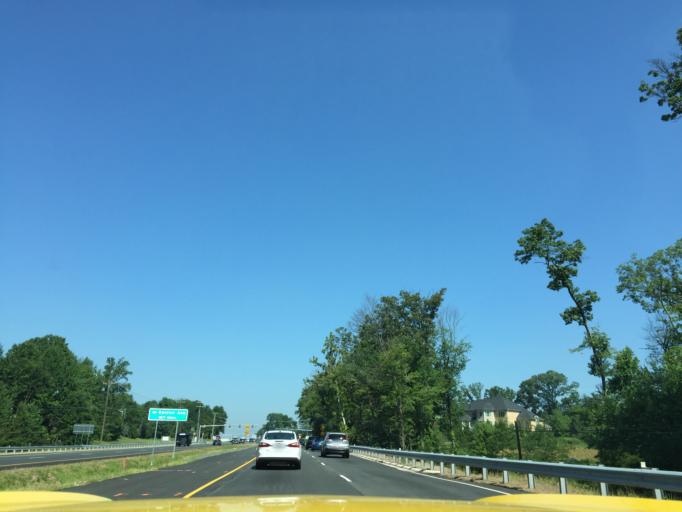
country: US
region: Virginia
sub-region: Fairfax County
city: Dranesville
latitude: 38.9973
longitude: -77.3400
